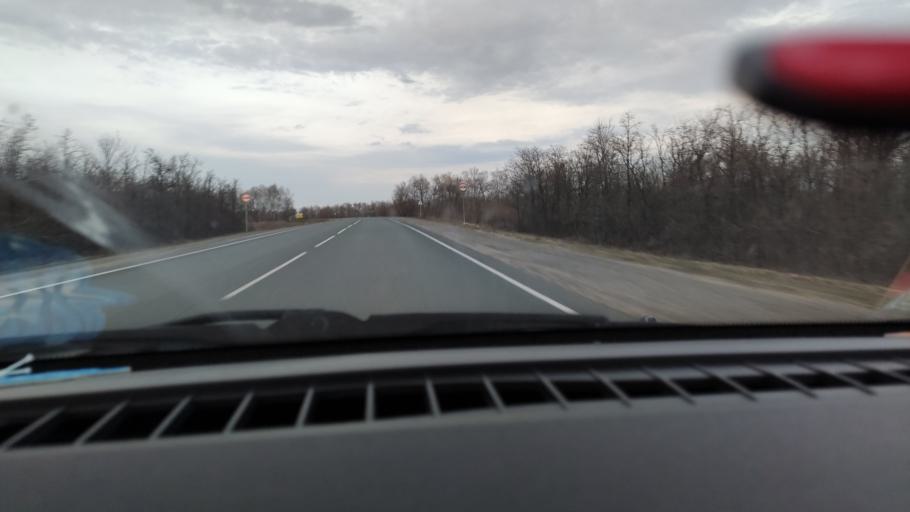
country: RU
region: Saratov
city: Sinodskoye
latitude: 51.9370
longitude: 46.5925
